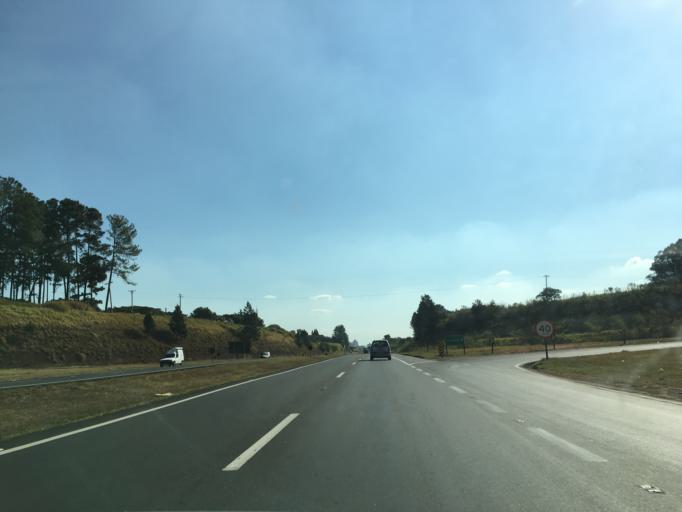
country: BR
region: Sao Paulo
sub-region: Piracicaba
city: Piracicaba
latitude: -22.7215
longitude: -47.6077
